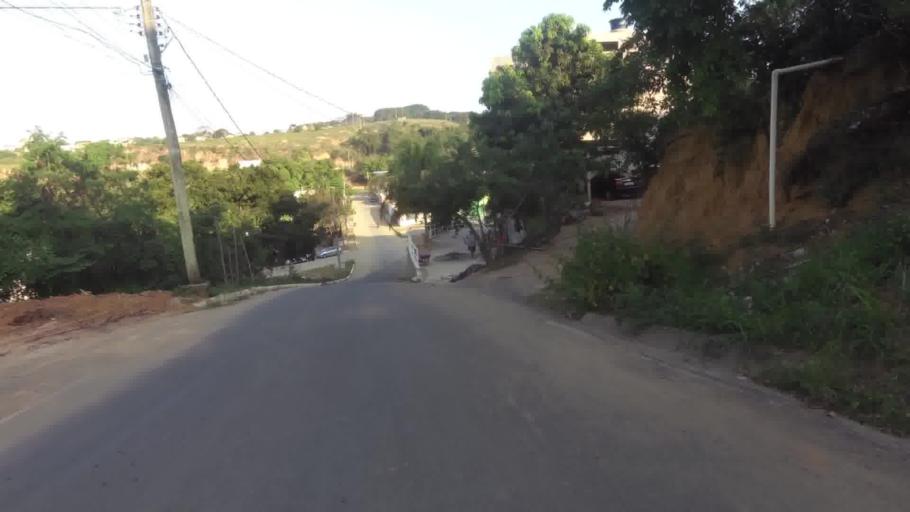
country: BR
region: Espirito Santo
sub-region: Piuma
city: Piuma
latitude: -20.8338
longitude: -40.7188
